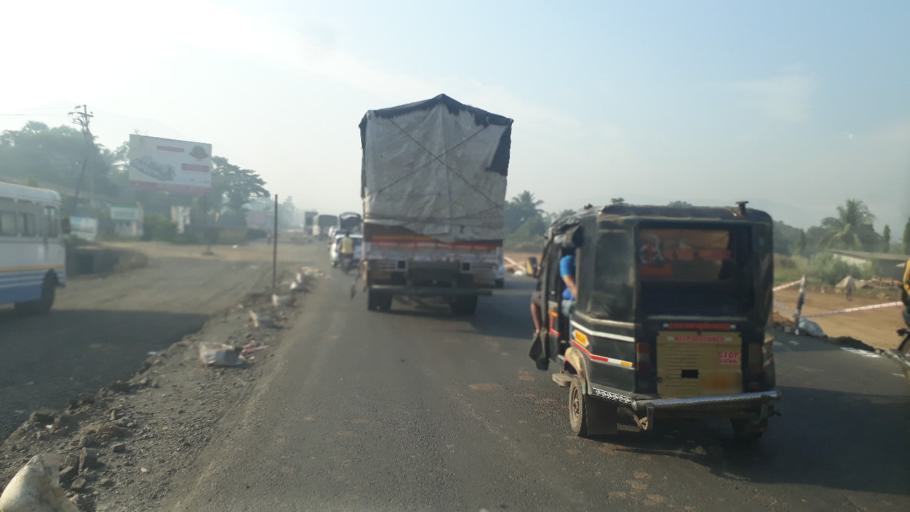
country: IN
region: Maharashtra
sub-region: Raigarh
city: Kalundri
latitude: 18.9308
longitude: 73.1274
